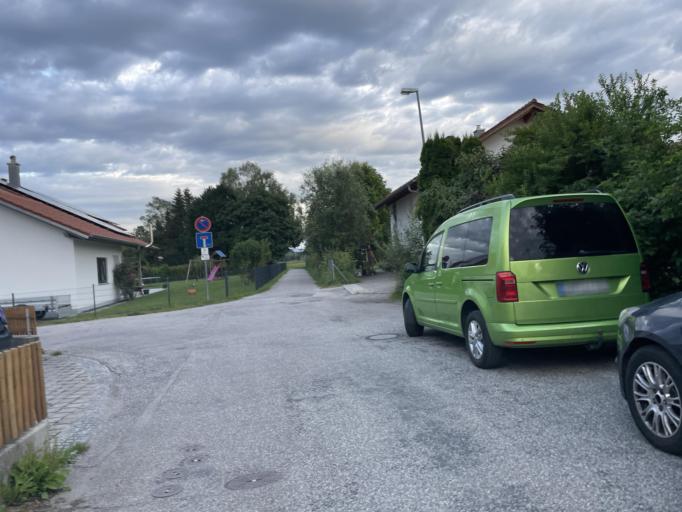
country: DE
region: Bavaria
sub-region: Upper Bavaria
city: Peissenberg
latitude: 47.7840
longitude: 11.0595
